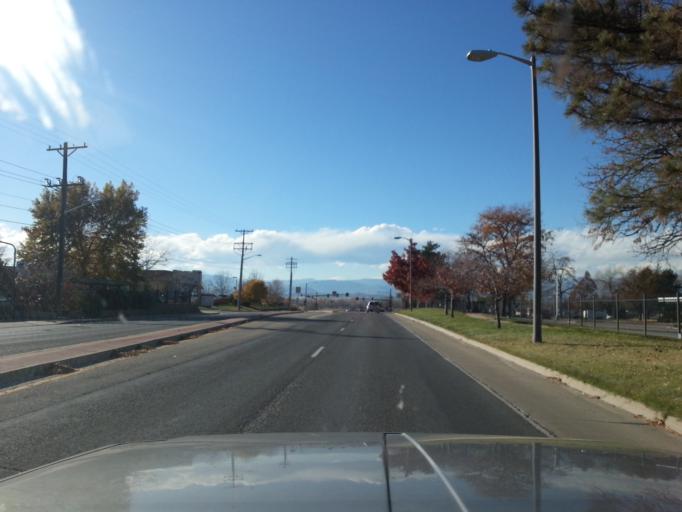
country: US
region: Colorado
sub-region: Larimer County
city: Loveland
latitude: 40.3784
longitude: -105.0928
